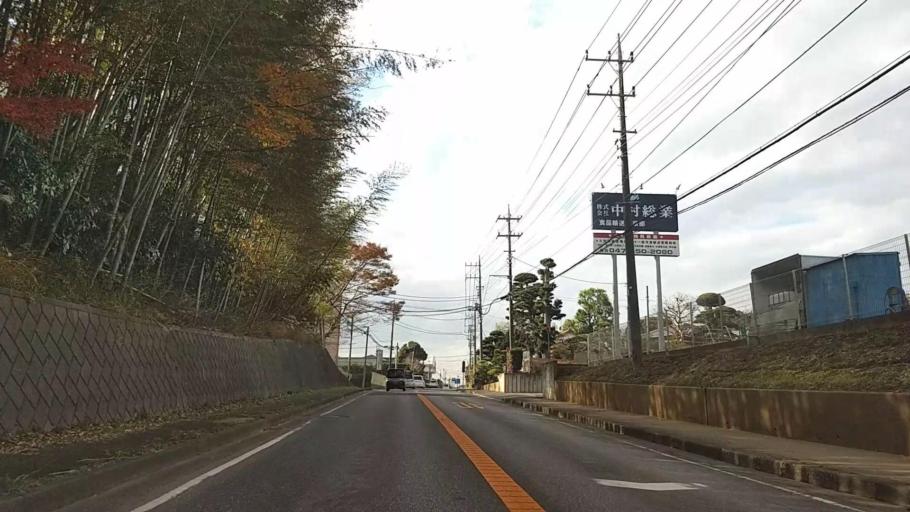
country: JP
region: Chiba
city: Oami
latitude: 35.5756
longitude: 140.3024
